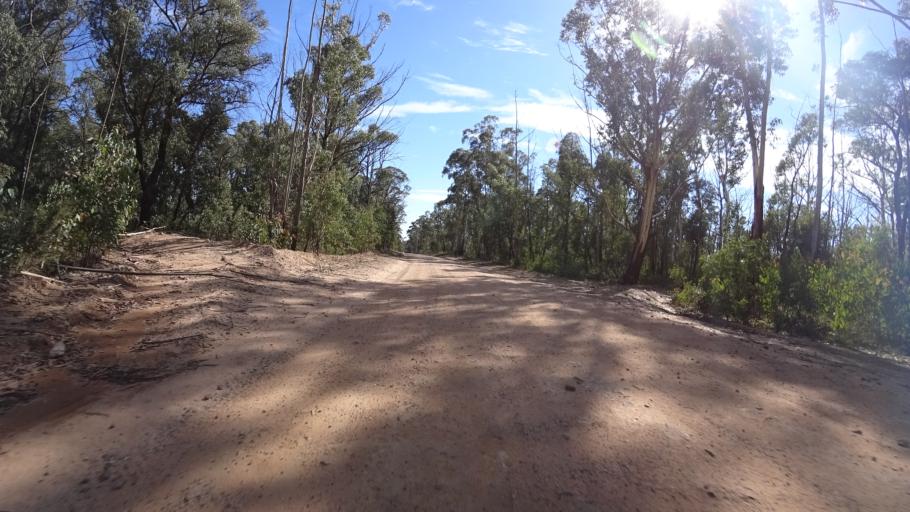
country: AU
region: New South Wales
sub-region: Lithgow
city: Lithgow
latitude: -33.4275
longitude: 150.1999
